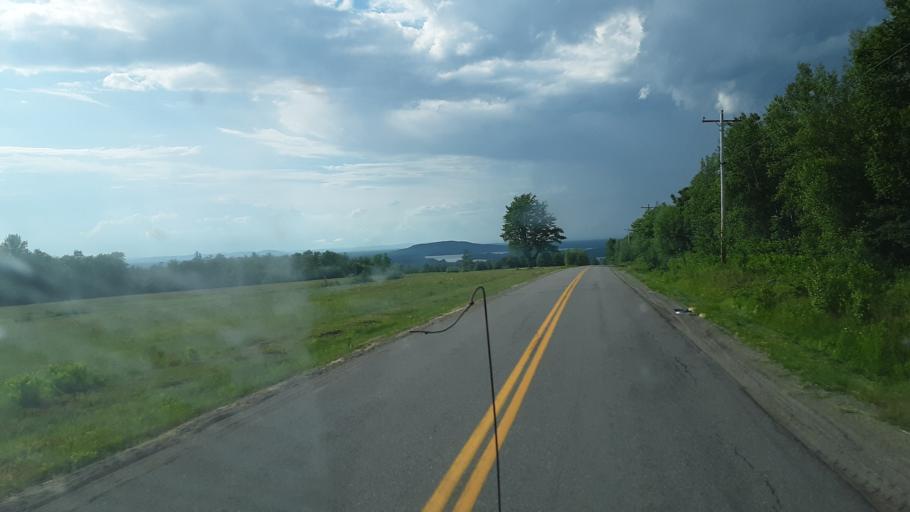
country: US
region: Maine
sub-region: Washington County
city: Calais
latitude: 45.0932
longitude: -67.5065
